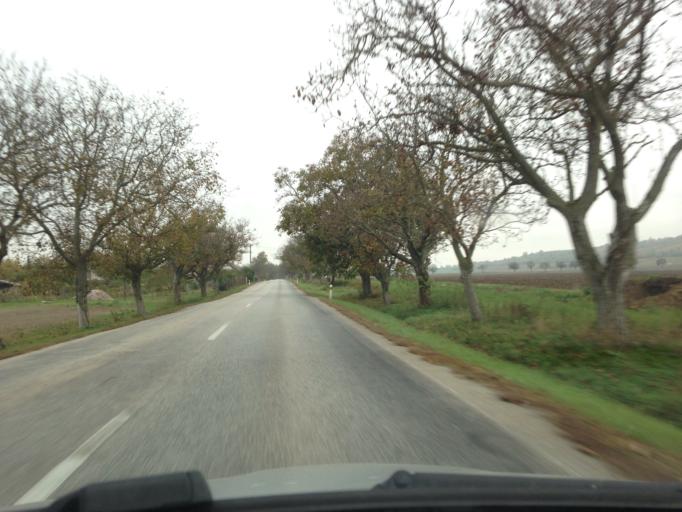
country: HU
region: Komarom-Esztergom
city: Nyergesujfalu
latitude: 47.8107
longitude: 18.6089
